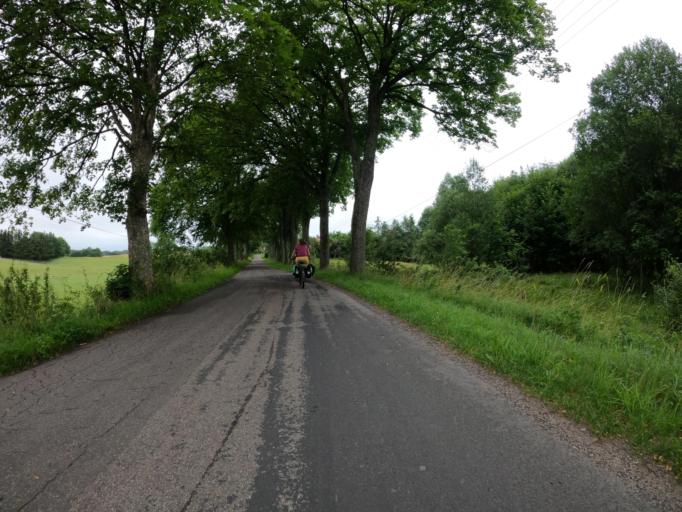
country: PL
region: West Pomeranian Voivodeship
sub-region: Powiat szczecinecki
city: Grzmiaca
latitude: 53.8967
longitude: 16.5026
